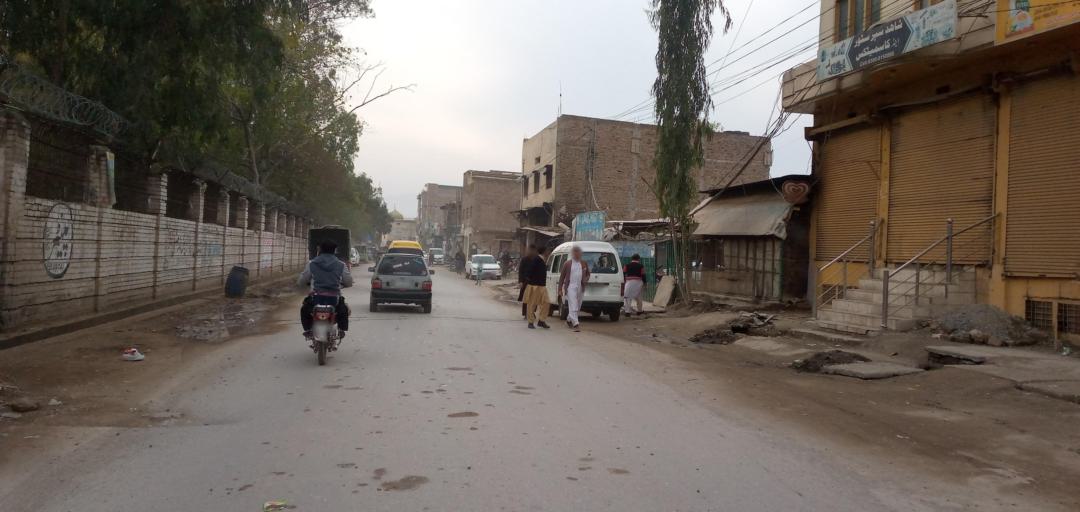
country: PK
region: Khyber Pakhtunkhwa
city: Peshawar
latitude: 34.0231
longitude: 71.4882
